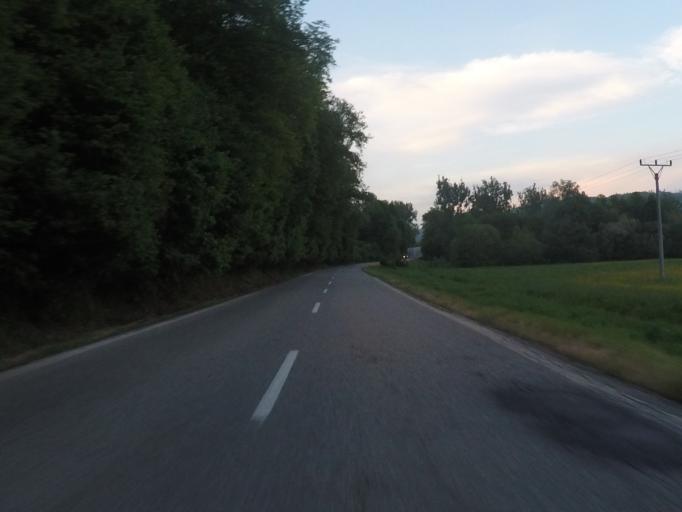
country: SK
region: Banskobystricky
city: Tisovec
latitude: 48.5302
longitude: 19.9510
